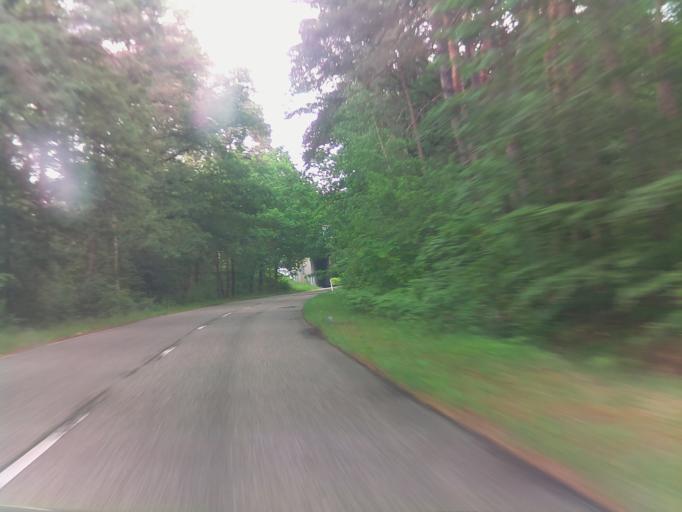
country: DE
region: Rheinland-Pfalz
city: Schifferstadt
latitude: 49.3535
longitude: 8.3877
